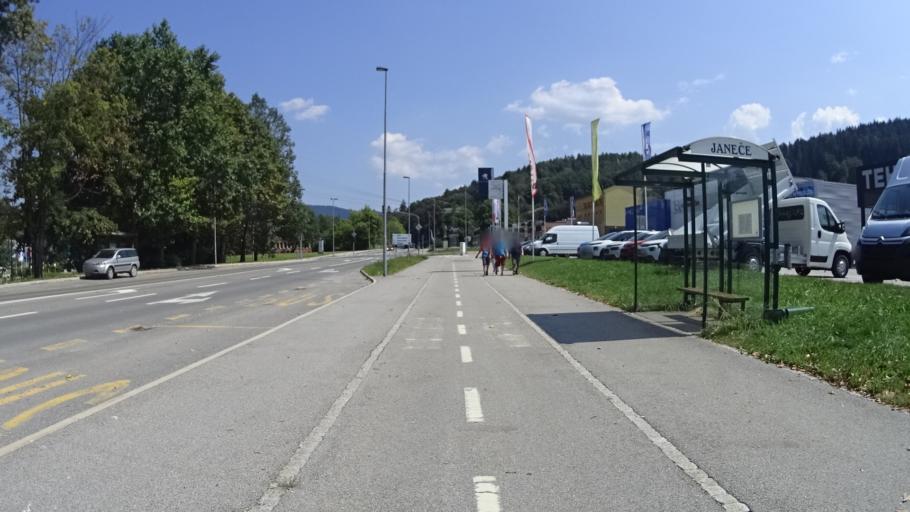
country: SI
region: Ravne na Koroskem
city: Ravne na Koroskem
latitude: 46.5436
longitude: 14.9485
